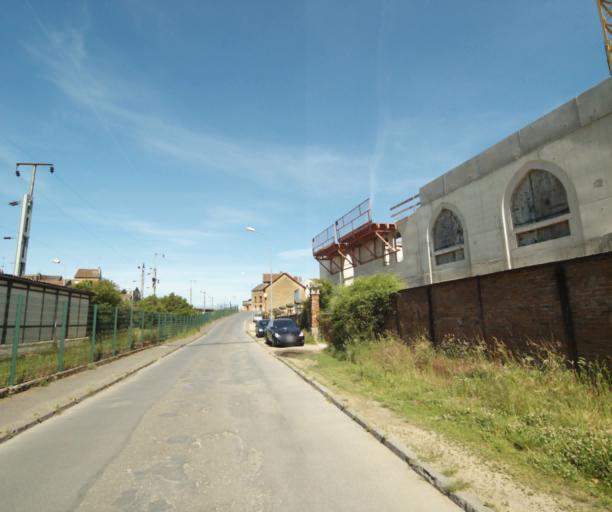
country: FR
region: Champagne-Ardenne
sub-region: Departement des Ardennes
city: Villers-Semeuse
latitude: 49.7528
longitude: 4.7336
